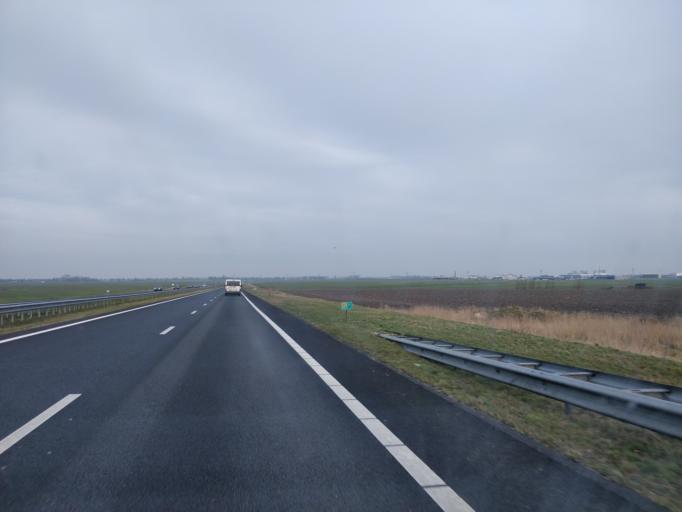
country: NL
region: Friesland
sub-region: Gemeente Leeuwarden
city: Goutum
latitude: 53.1695
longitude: 5.7628
